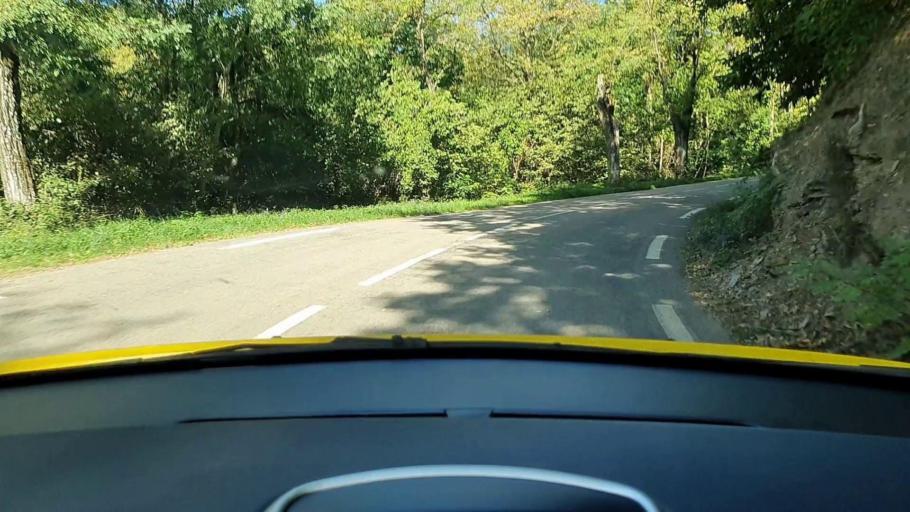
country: FR
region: Languedoc-Roussillon
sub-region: Departement du Gard
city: Le Vigan
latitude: 43.9702
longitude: 3.4147
